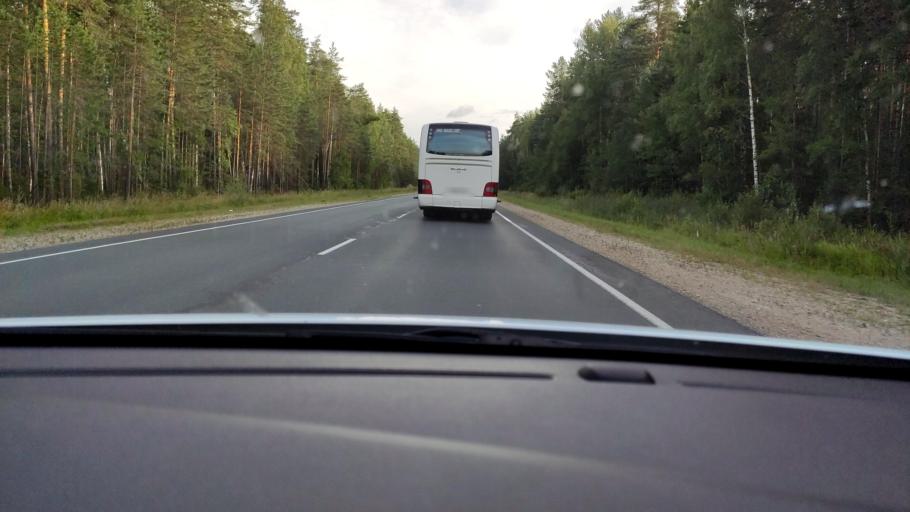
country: RU
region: Mariy-El
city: Suslonger
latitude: 56.2906
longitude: 48.2334
